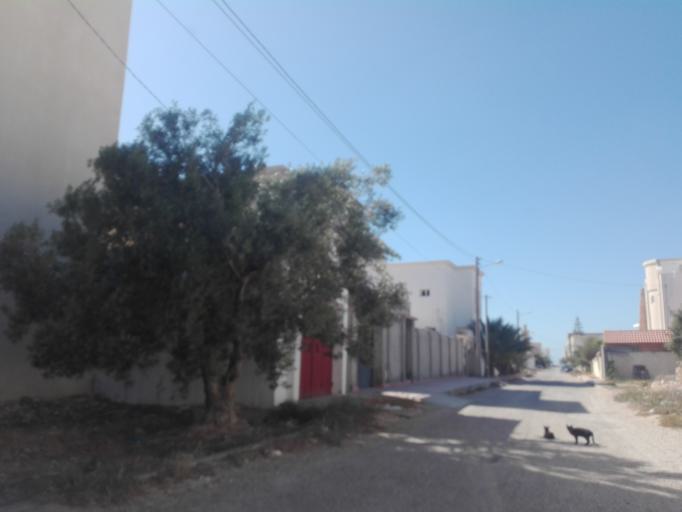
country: TN
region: Safaqis
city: Al Qarmadah
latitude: 34.7079
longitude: 11.2008
